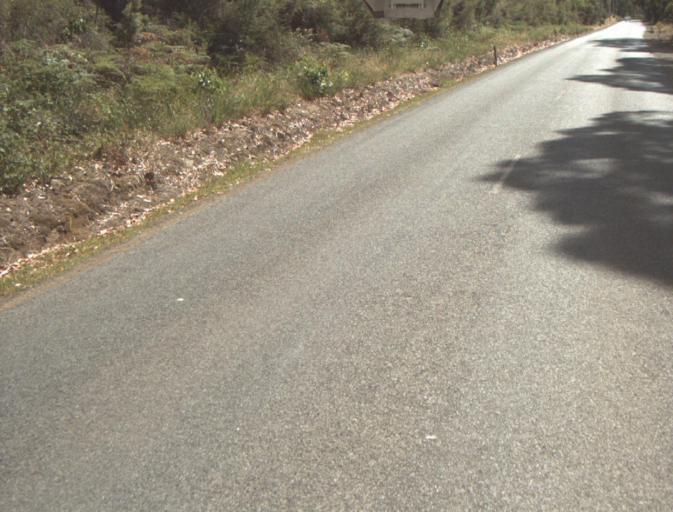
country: AU
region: Tasmania
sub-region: Launceston
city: Mayfield
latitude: -41.2191
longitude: 147.2076
